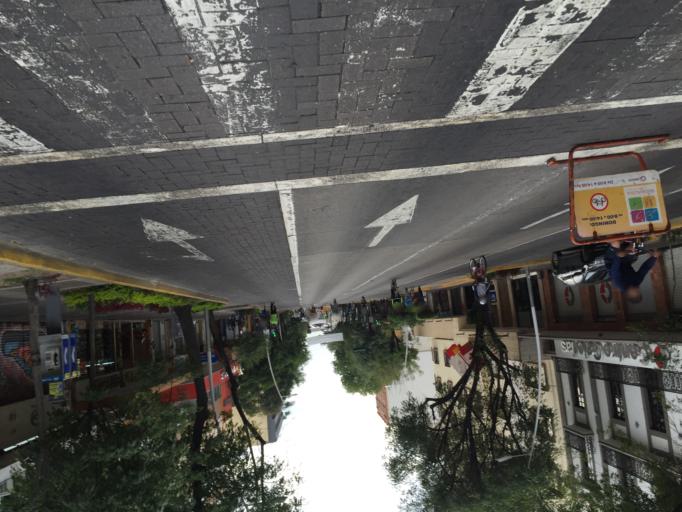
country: MX
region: Jalisco
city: Guadalajara
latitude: 20.6752
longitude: -103.3457
